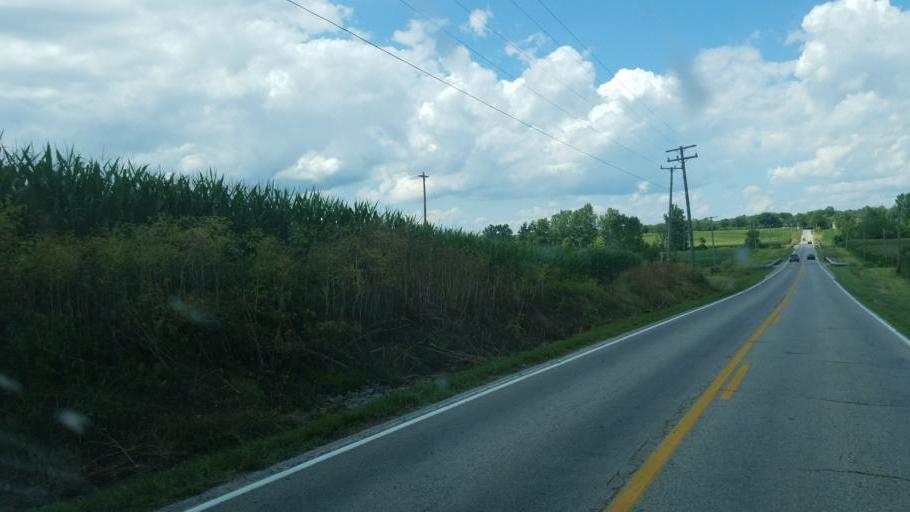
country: US
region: Ohio
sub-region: Highland County
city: Greenfield
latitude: 39.3311
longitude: -83.3988
